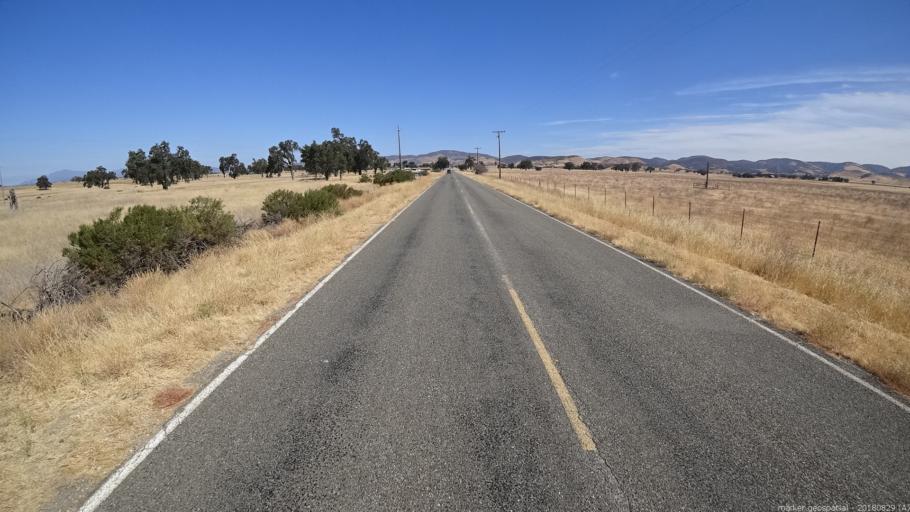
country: US
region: California
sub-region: Monterey County
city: King City
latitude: 35.9325
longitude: -121.0822
